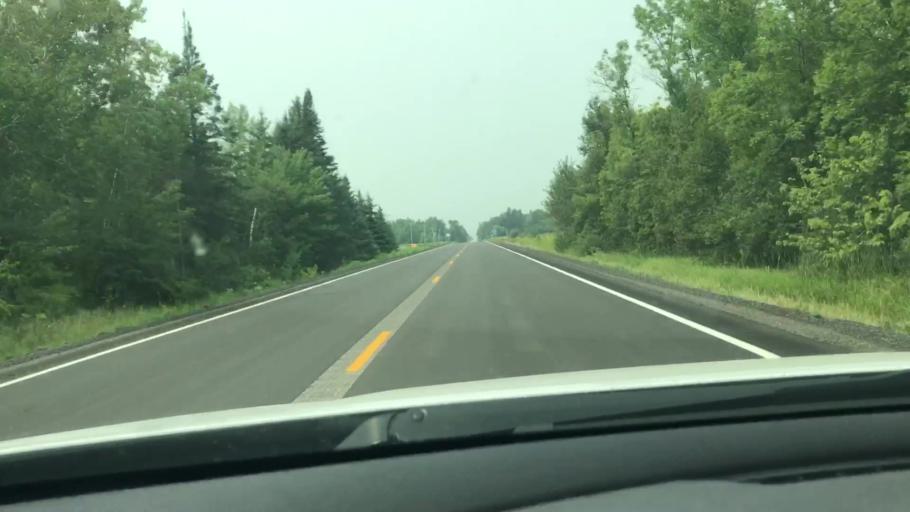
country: US
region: Minnesota
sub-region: Itasca County
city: Cohasset
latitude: 47.3538
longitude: -93.8462
